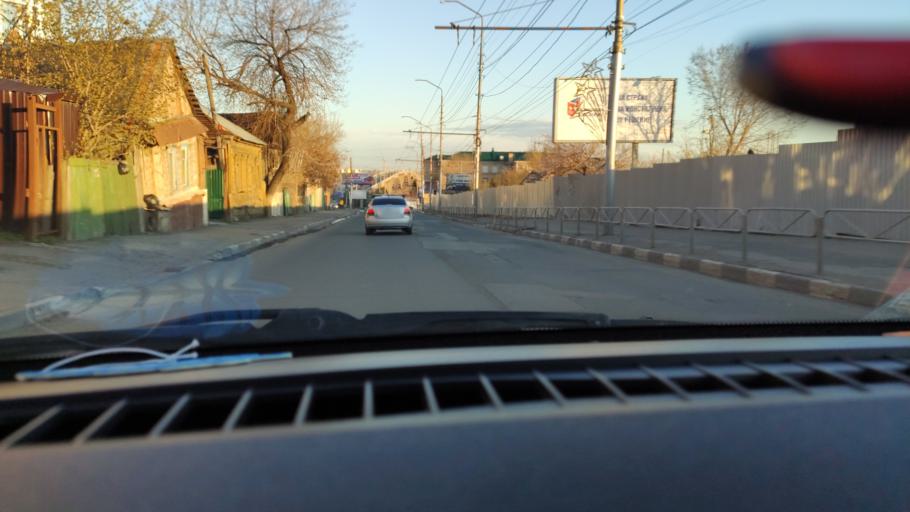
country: RU
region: Saratov
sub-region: Saratovskiy Rayon
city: Saratov
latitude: 51.5287
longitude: 46.0627
